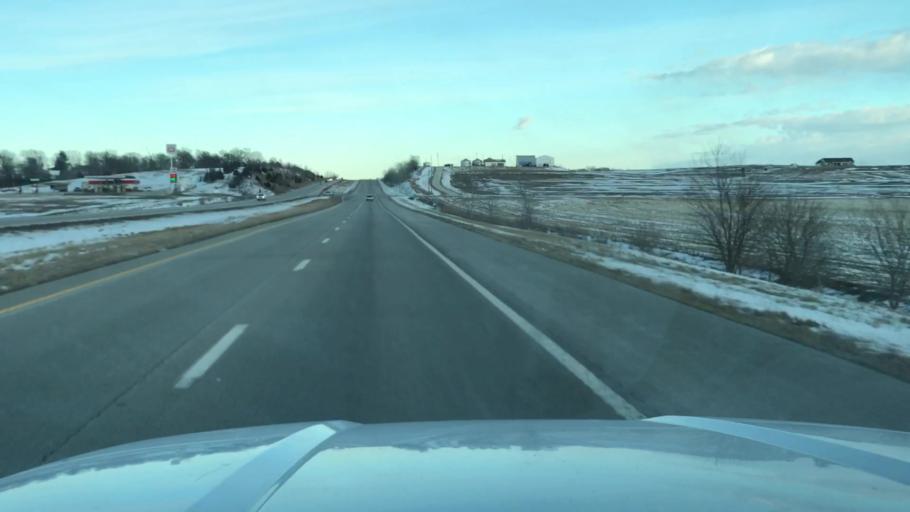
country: US
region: Missouri
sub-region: Buchanan County
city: Saint Joseph
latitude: 39.7477
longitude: -94.7154
